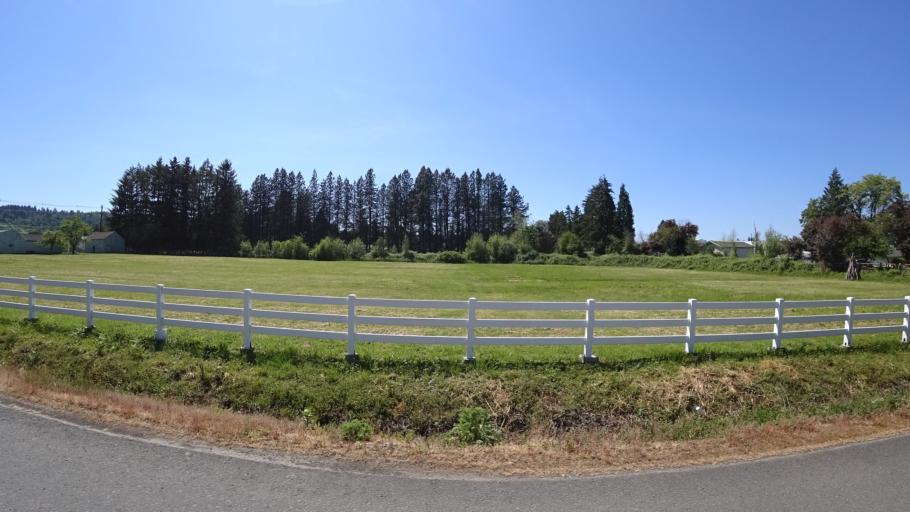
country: US
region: Oregon
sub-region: Clackamas County
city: Happy Valley
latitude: 45.4631
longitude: -122.4875
